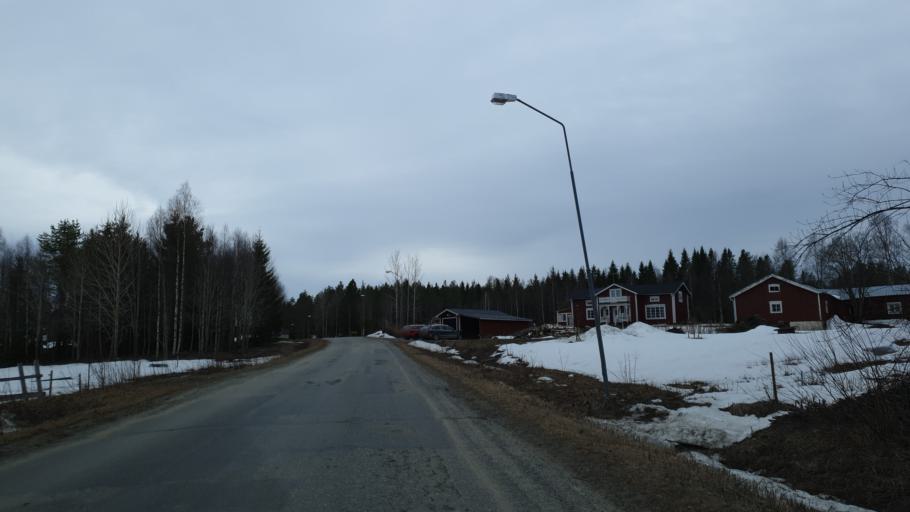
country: SE
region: Vaesterbotten
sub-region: Robertsfors Kommun
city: Robertsfors
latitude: 64.3964
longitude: 21.0023
